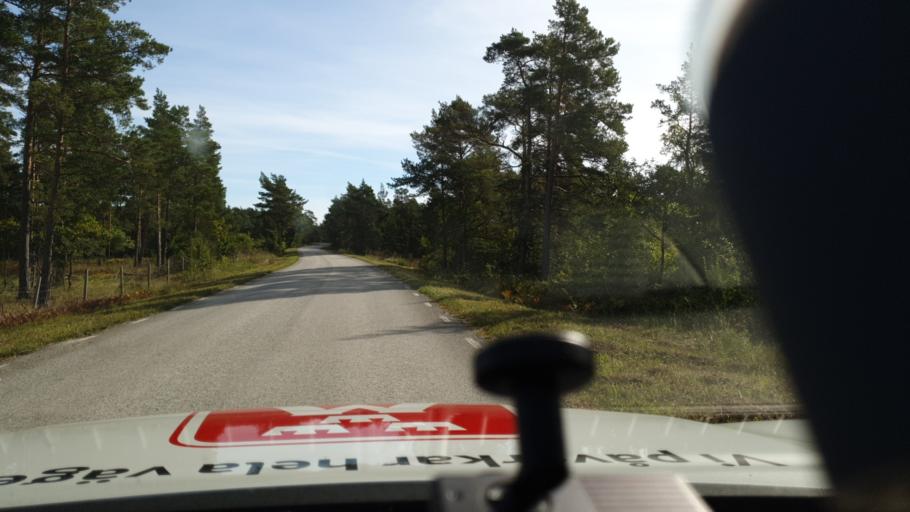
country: SE
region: Gotland
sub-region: Gotland
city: Slite
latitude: 57.8533
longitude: 18.7341
